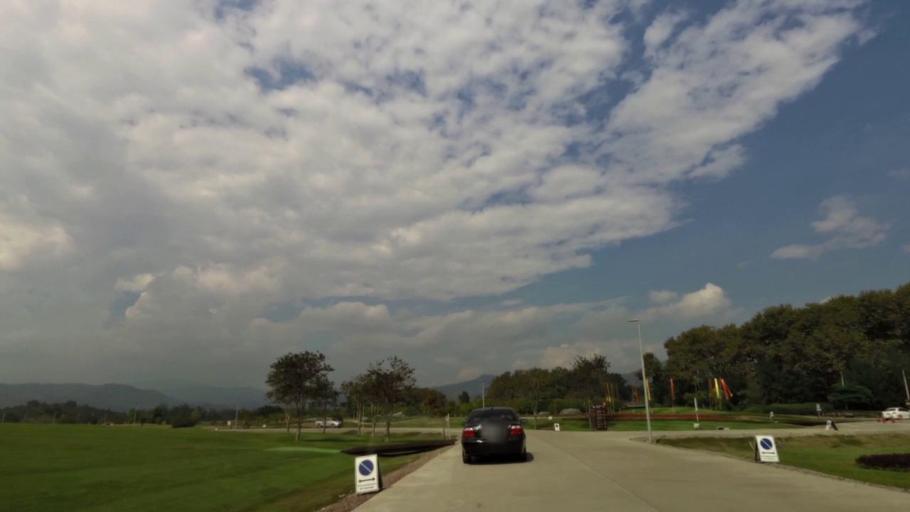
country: TH
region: Chiang Rai
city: Mae Lao
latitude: 19.8531
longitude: 99.7441
